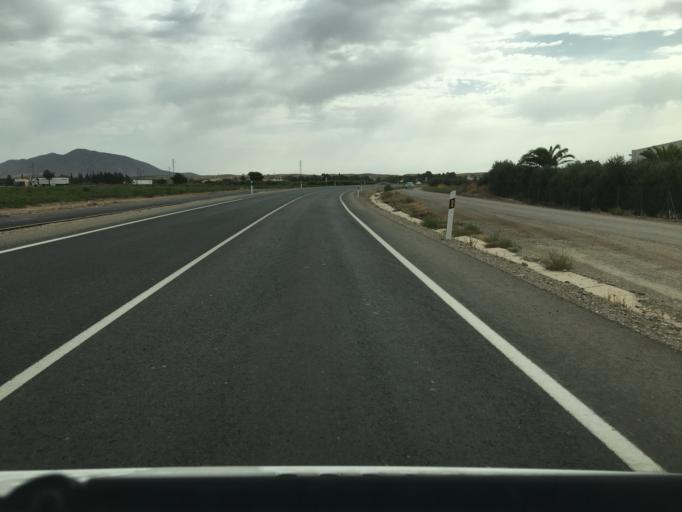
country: ES
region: Andalusia
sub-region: Provincia de Almeria
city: Huercal-Overa
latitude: 37.4164
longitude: -1.8900
